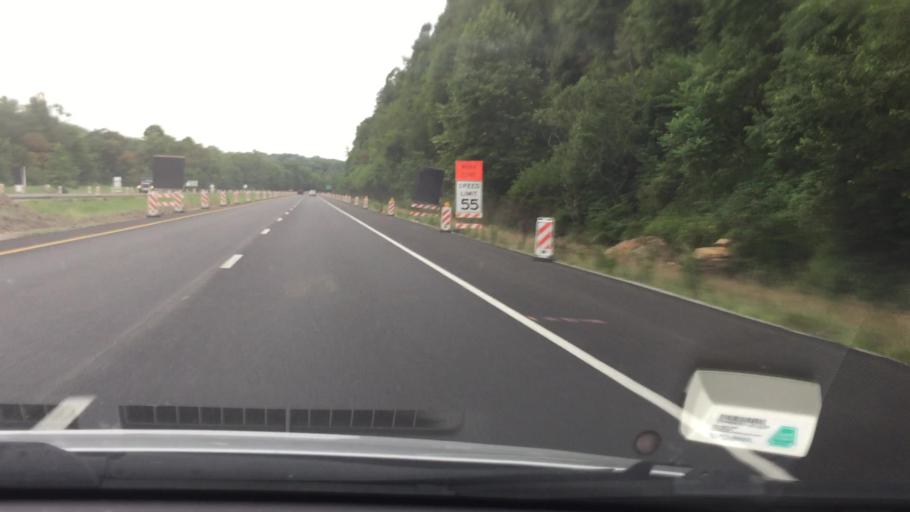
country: US
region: Pennsylvania
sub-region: Armstrong County
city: Freeport
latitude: 40.6501
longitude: -79.7235
